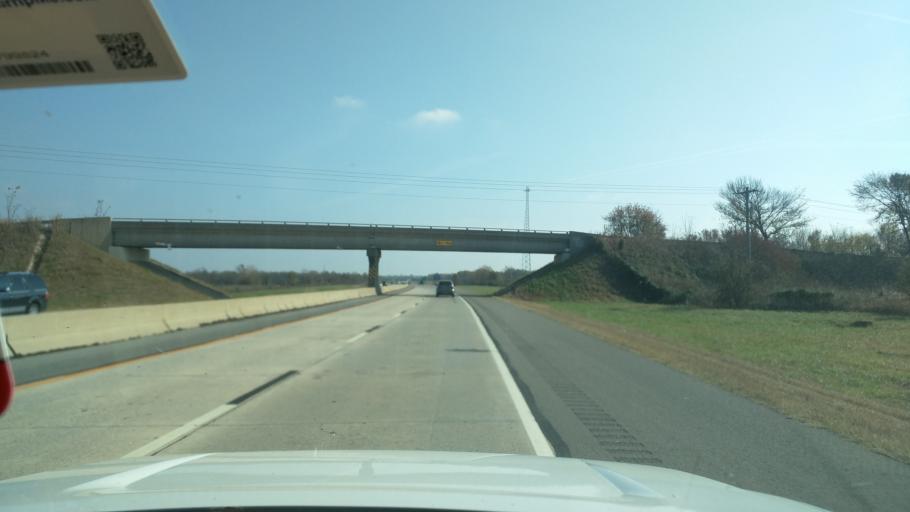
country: US
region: Oklahoma
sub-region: Wagoner County
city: Wagoner
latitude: 35.8609
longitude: -95.4475
